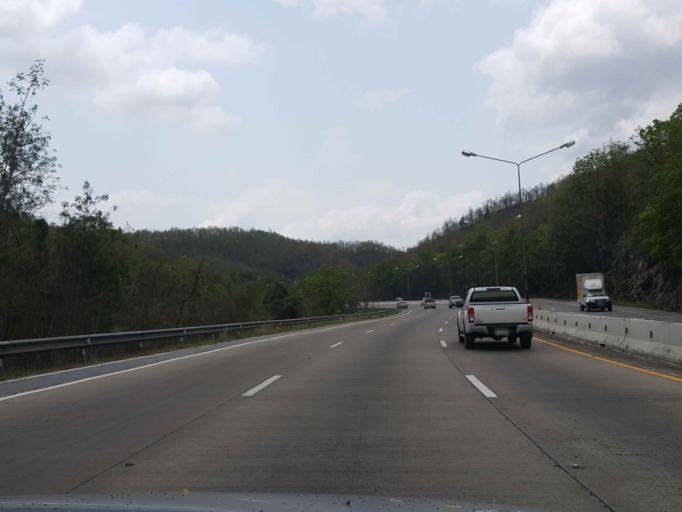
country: TH
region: Lamphun
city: Mae Tha
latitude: 18.4971
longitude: 99.1358
